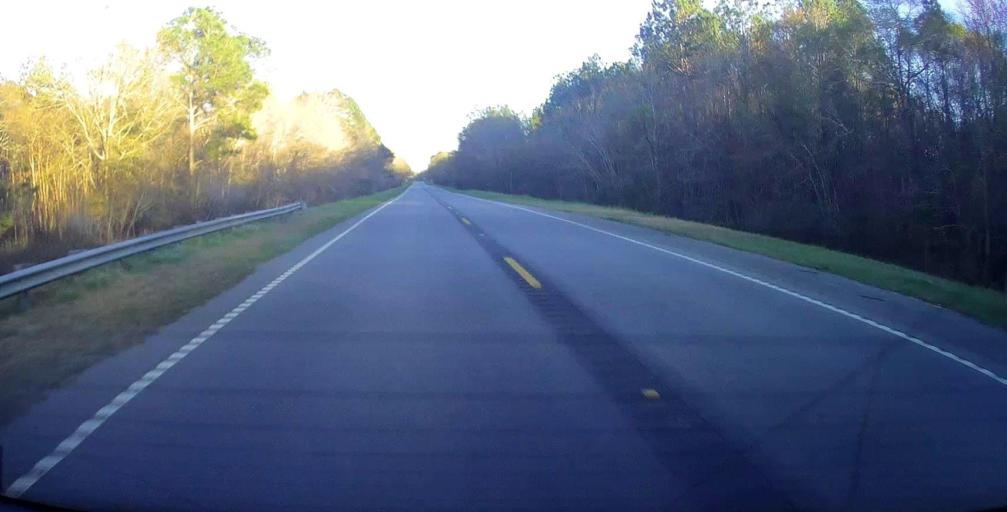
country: US
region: Georgia
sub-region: Wilcox County
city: Rochelle
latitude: 31.9481
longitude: -83.5624
